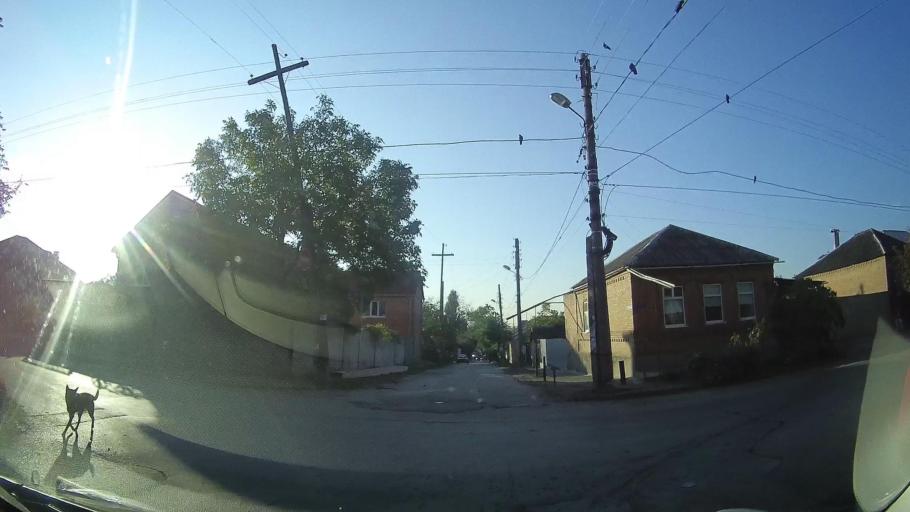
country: RU
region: Rostov
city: Severnyy
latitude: 47.2681
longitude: 39.6732
